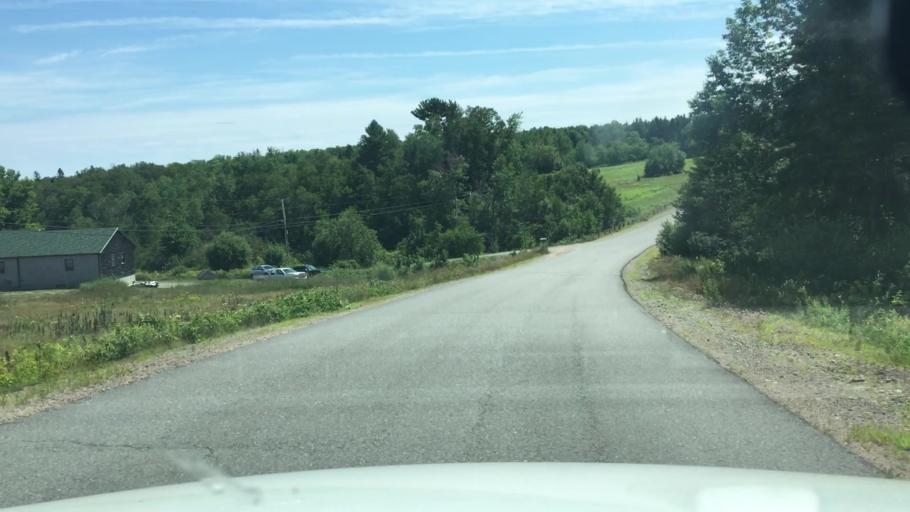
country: CA
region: New Brunswick
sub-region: Charlotte County
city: Saint Andrews
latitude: 44.9947
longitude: -67.0658
